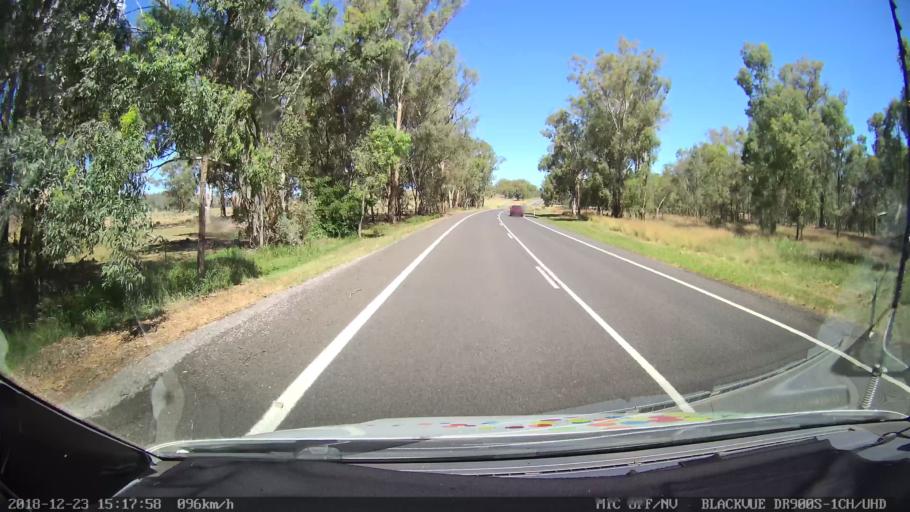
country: AU
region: New South Wales
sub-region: Tamworth Municipality
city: Manilla
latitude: -30.8127
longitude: 150.7666
